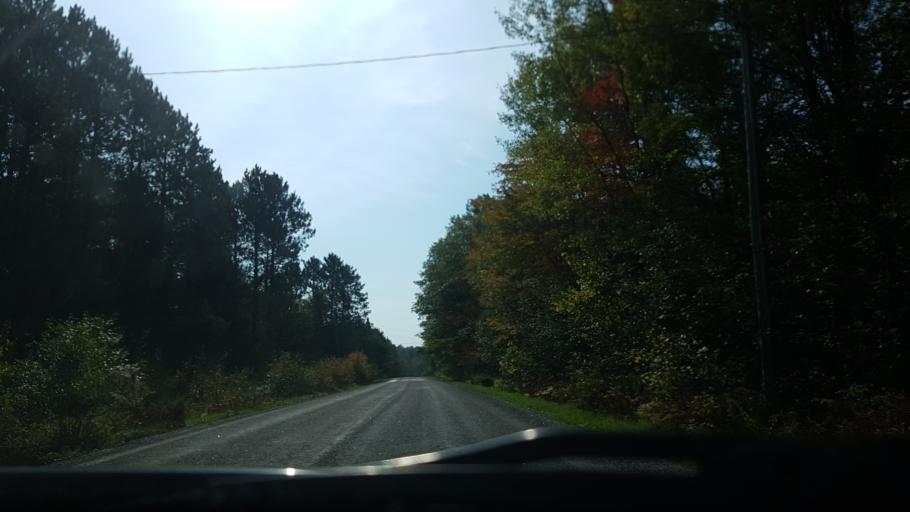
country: CA
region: Ontario
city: Gravenhurst
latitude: 44.8010
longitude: -79.2092
